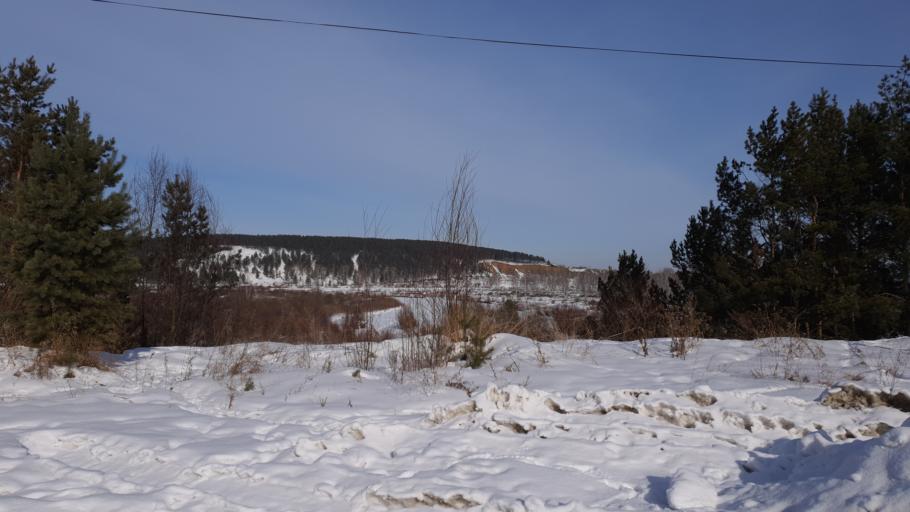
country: RU
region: Irkutsk
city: Tulun
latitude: 54.5356
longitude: 100.5784
